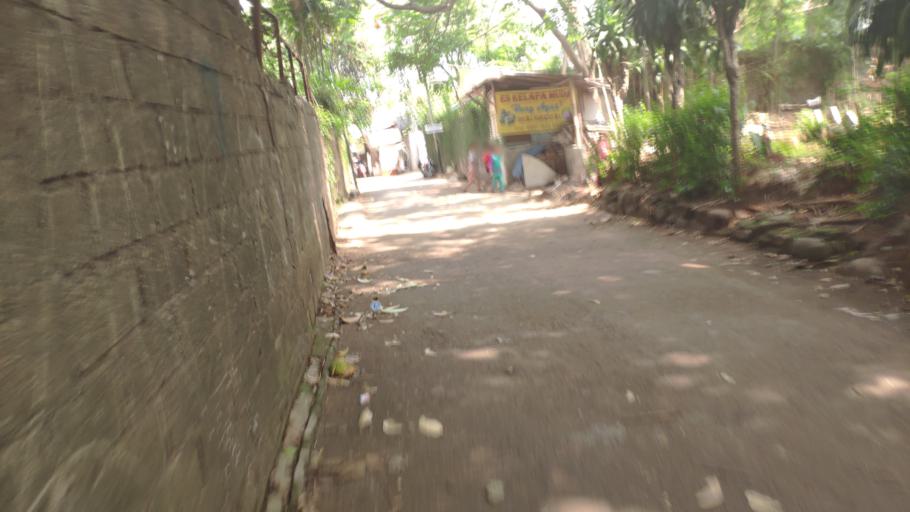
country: ID
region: Jakarta Raya
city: Jakarta
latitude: -6.2678
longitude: 106.8274
